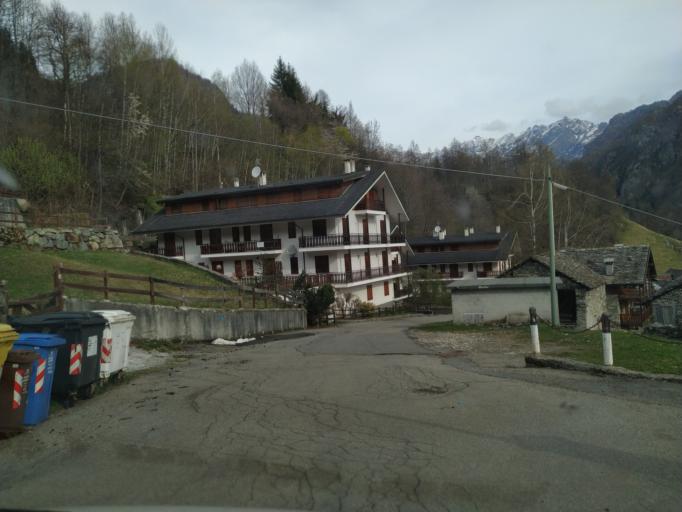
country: IT
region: Piedmont
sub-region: Provincia di Vercelli
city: Piode
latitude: 45.7683
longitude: 8.0489
